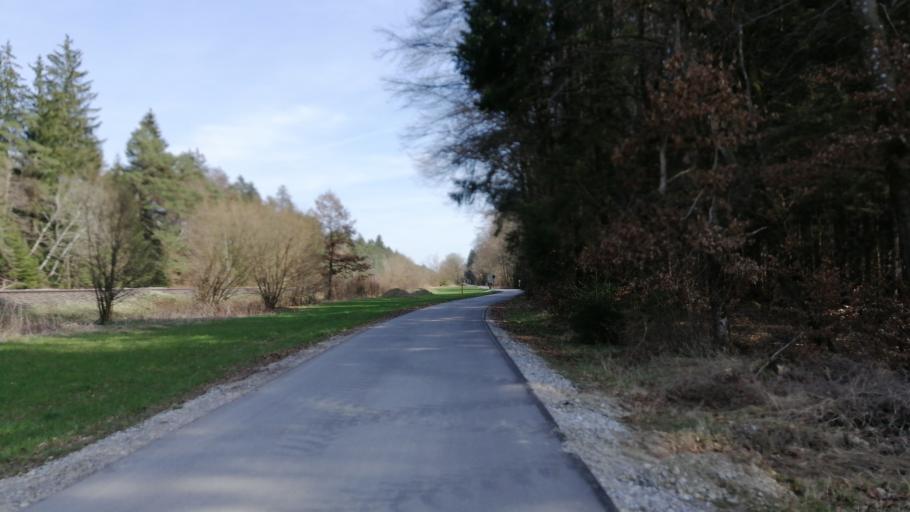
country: DE
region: Bavaria
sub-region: Upper Bavaria
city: Oberhaching
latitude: 48.0030
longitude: 11.6021
